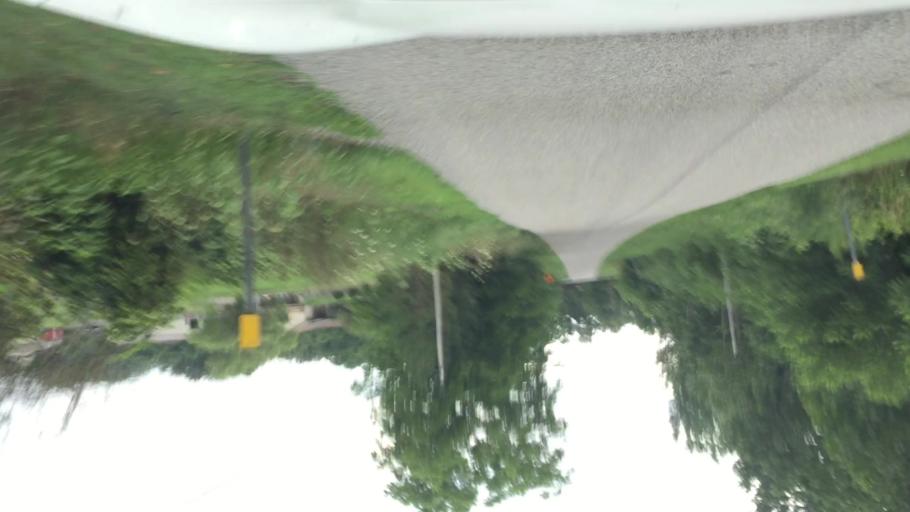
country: US
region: Ohio
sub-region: Champaign County
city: North Lewisburg
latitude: 40.2478
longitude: -83.5218
